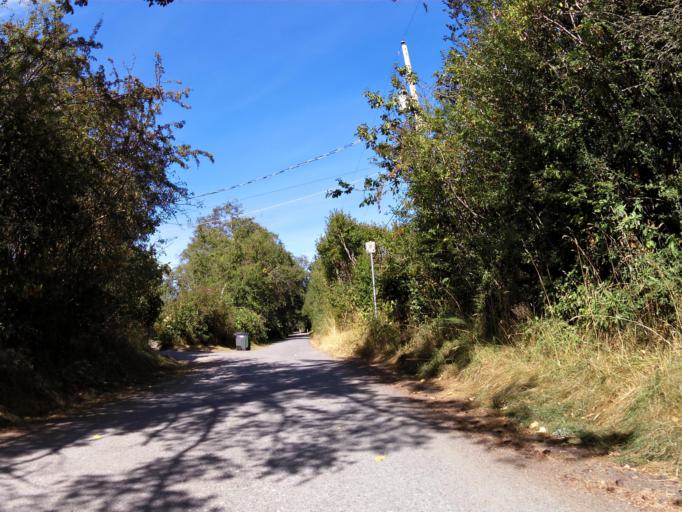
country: CA
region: British Columbia
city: Victoria
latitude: 48.5402
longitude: -123.3813
